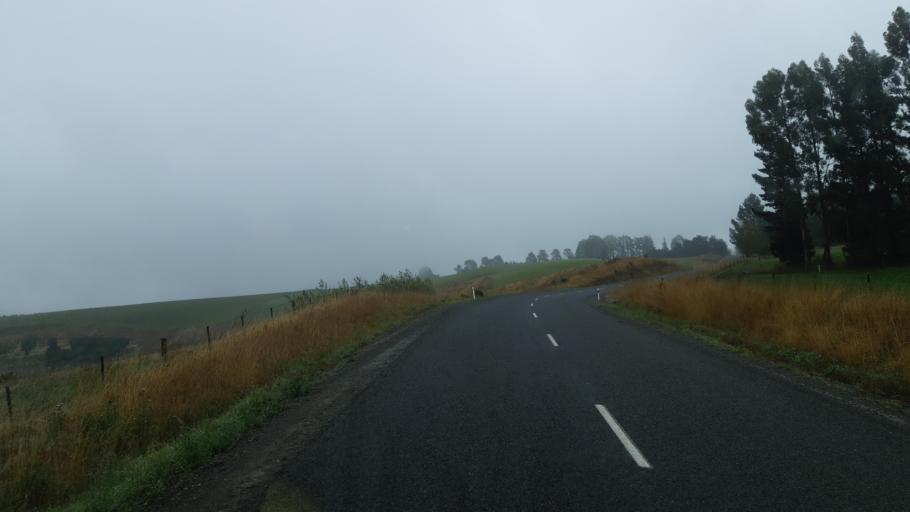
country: NZ
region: Otago
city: Oamaru
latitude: -44.9400
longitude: 170.7508
